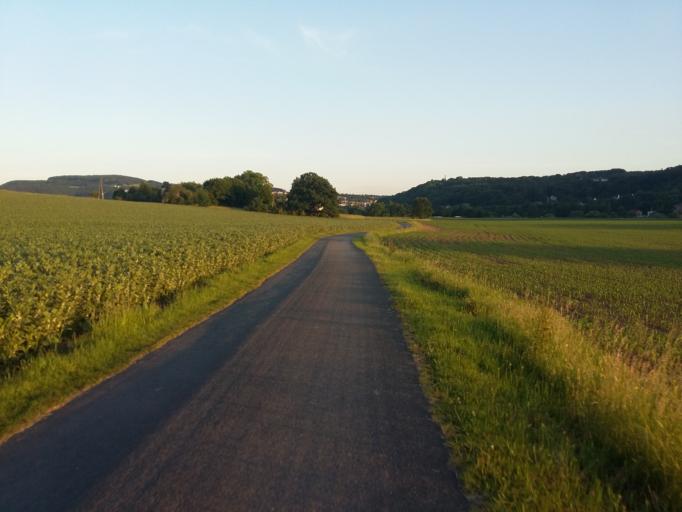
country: DE
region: North Rhine-Westphalia
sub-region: Regierungsbezirk Detmold
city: Vlotho
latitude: 52.1890
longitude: 8.8650
